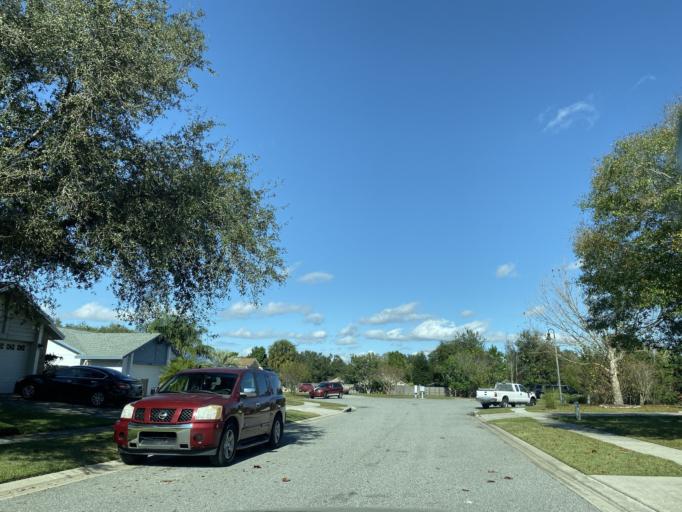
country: US
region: Florida
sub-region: Seminole County
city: Goldenrod
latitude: 28.6208
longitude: -81.2625
